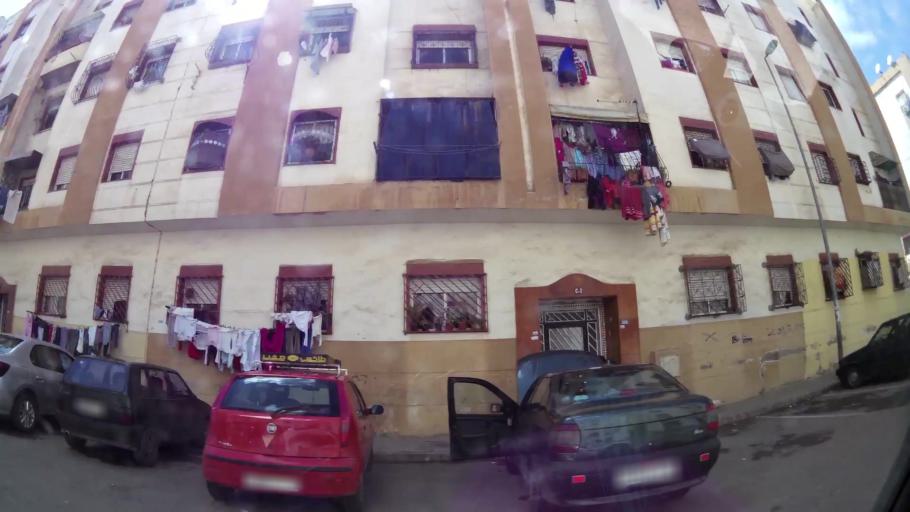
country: MA
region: Grand Casablanca
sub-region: Mediouna
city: Tit Mellil
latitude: 33.6006
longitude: -7.4789
